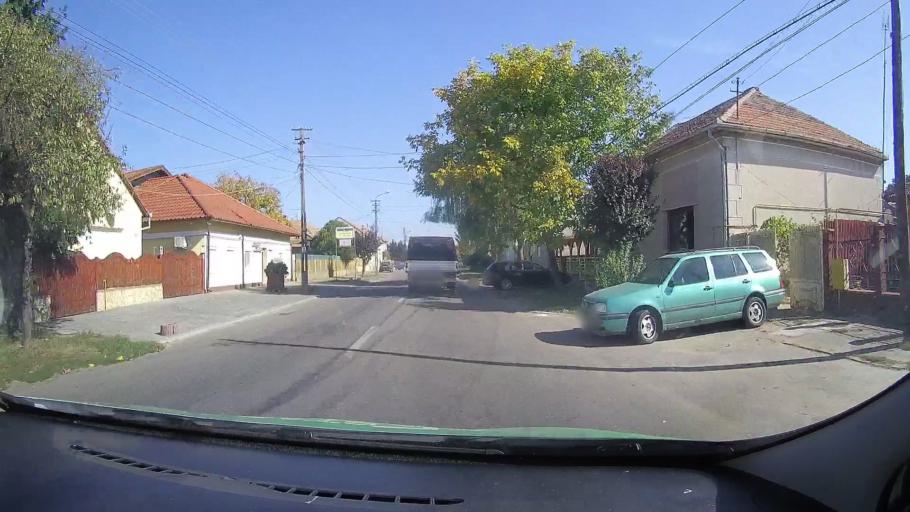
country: RO
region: Satu Mare
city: Carei
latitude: 47.6924
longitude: 22.4715
